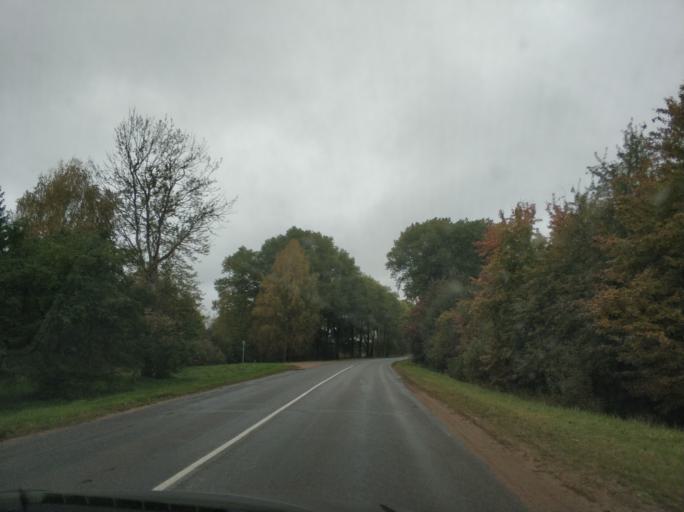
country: BY
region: Vitebsk
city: Polatsk
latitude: 55.4448
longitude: 28.9435
